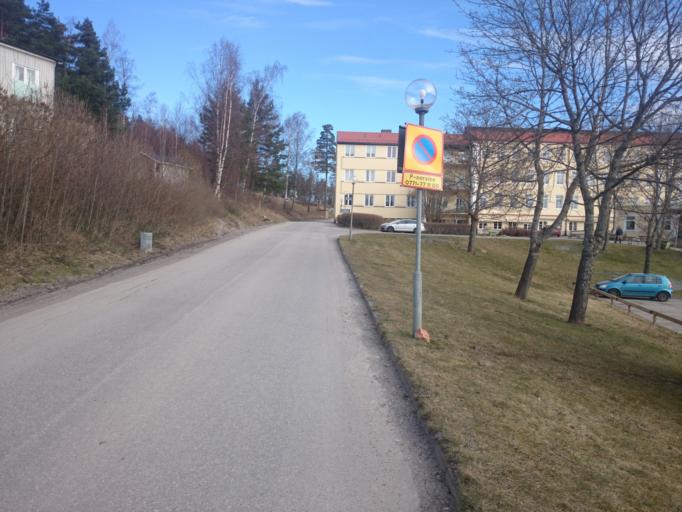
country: SE
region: Stockholm
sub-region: Botkyrka Kommun
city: Tumba
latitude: 59.2005
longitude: 17.8029
